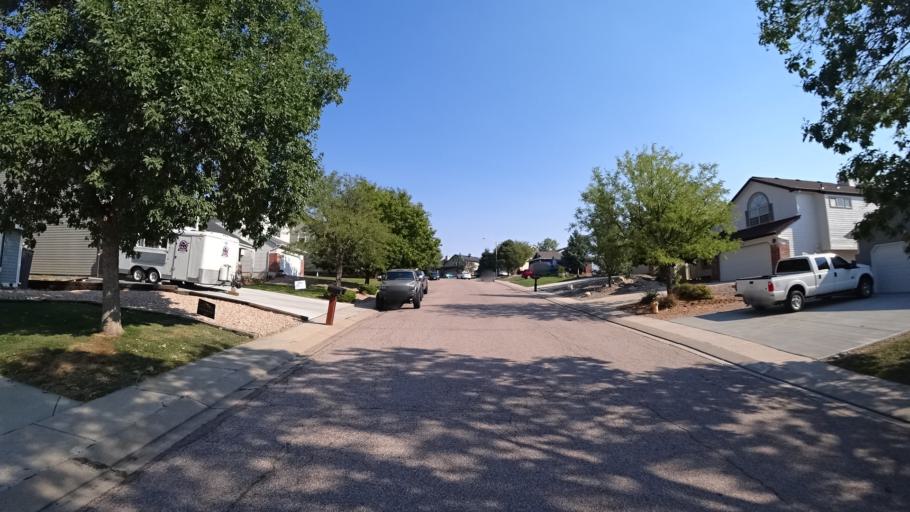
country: US
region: Colorado
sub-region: El Paso County
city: Stratmoor
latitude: 38.7796
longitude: -104.8015
